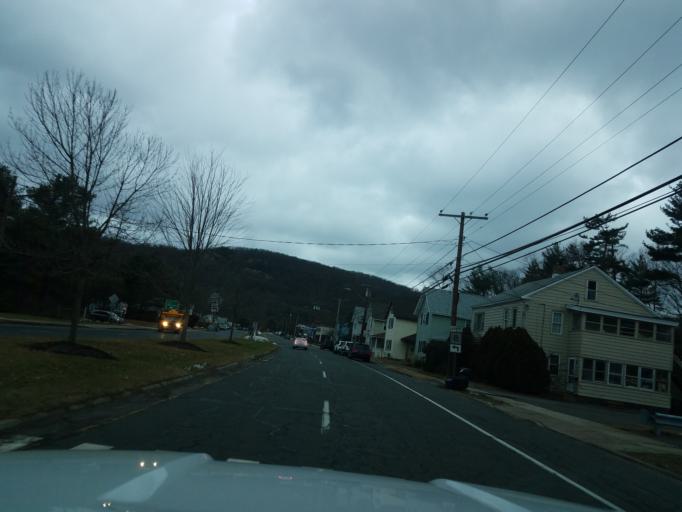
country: US
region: Connecticut
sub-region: New Haven County
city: Naugatuck
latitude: 41.4441
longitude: -73.0635
